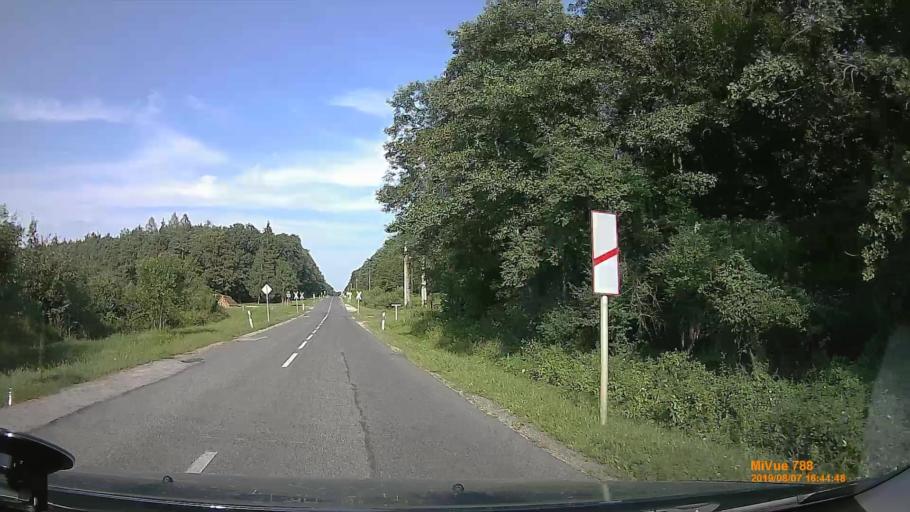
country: HU
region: Zala
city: Lenti
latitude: 46.6420
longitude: 16.6035
